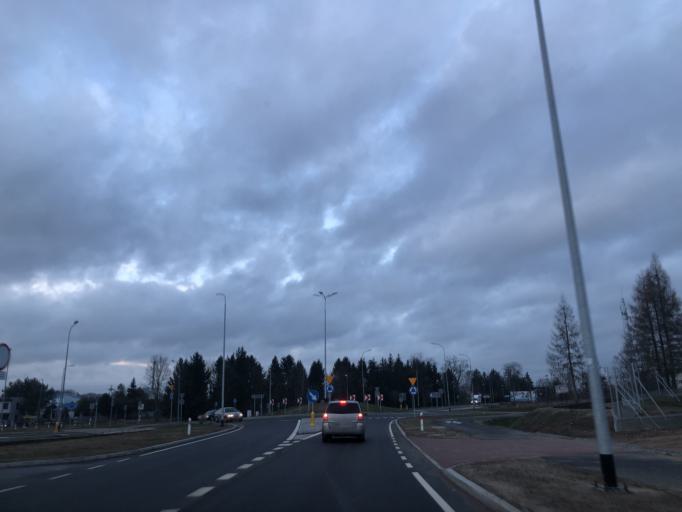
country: PL
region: Podlasie
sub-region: Lomza
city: Lomza
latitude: 53.1515
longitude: 22.0501
